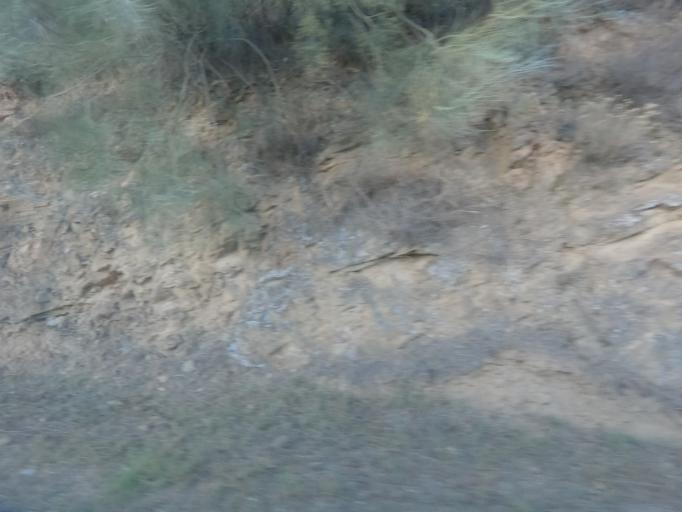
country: PT
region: Viseu
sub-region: Armamar
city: Armamar
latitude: 41.1628
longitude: -7.6817
